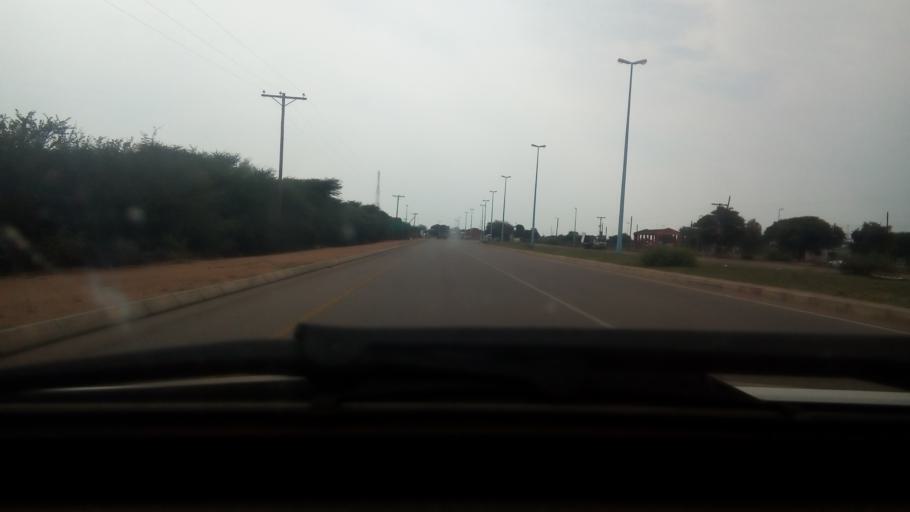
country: BW
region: South East
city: Gaborone
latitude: -24.7012
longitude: 26.0873
